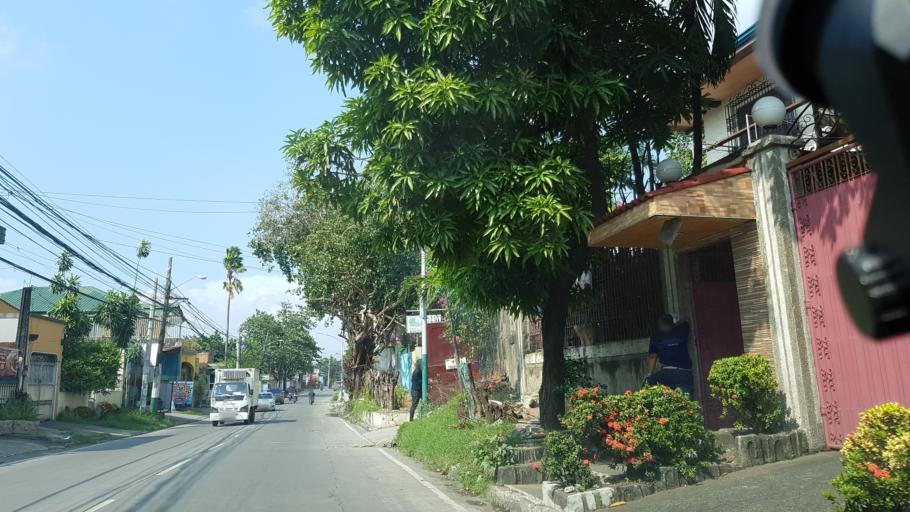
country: PH
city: Sambayanihan People's Village
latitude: 14.4813
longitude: 121.0305
